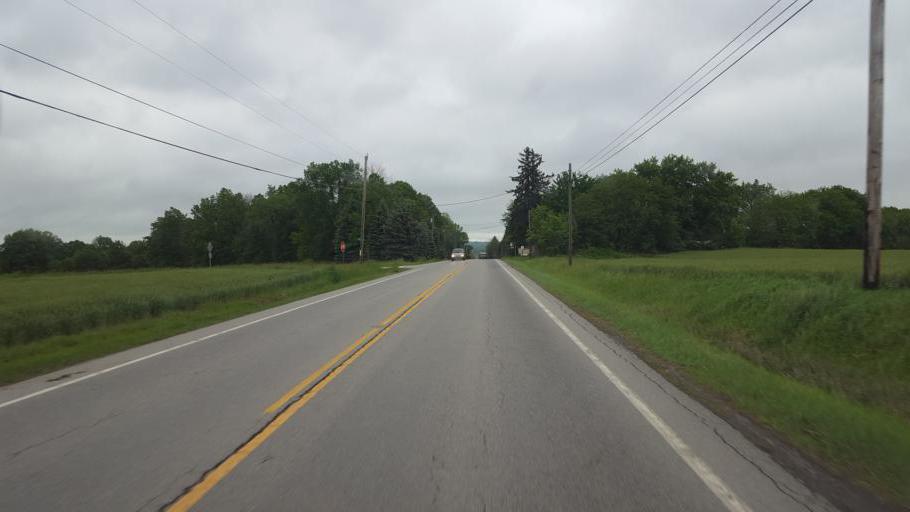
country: US
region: Ohio
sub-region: Wayne County
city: West Salem
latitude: 41.0003
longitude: -82.0689
